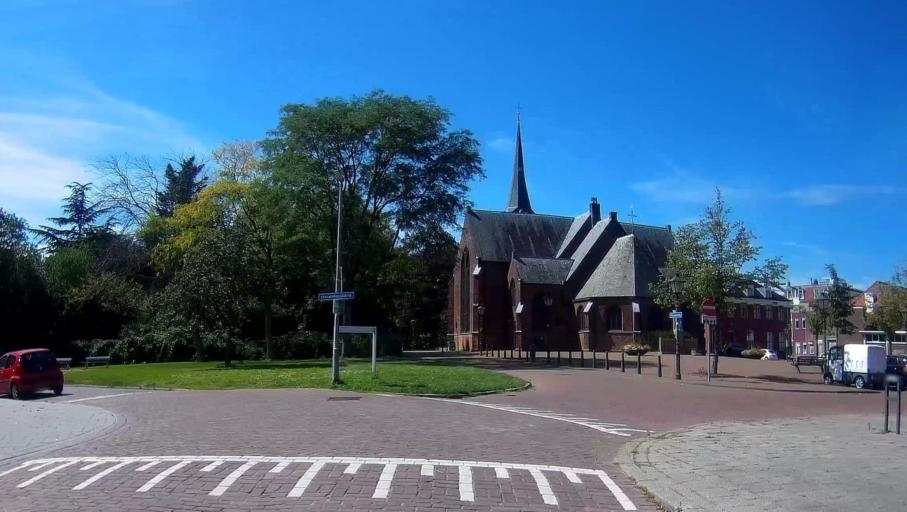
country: NL
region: South Holland
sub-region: Gemeente Rotterdam
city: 's-Gravenland
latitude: 51.9004
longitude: 4.5499
